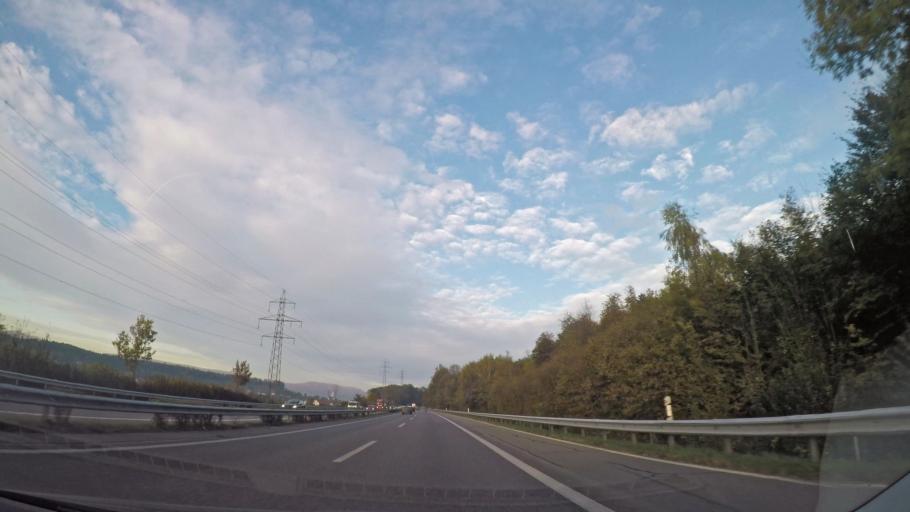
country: CH
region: Aargau
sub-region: Bezirk Aarau
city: Oberentfelden
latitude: 47.3571
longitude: 8.0637
